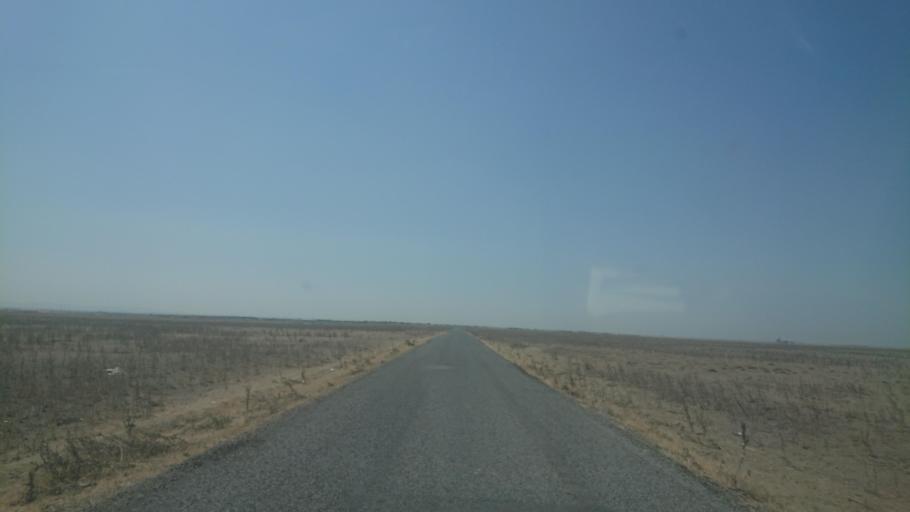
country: TR
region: Aksaray
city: Yesilova
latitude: 38.3163
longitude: 33.7406
